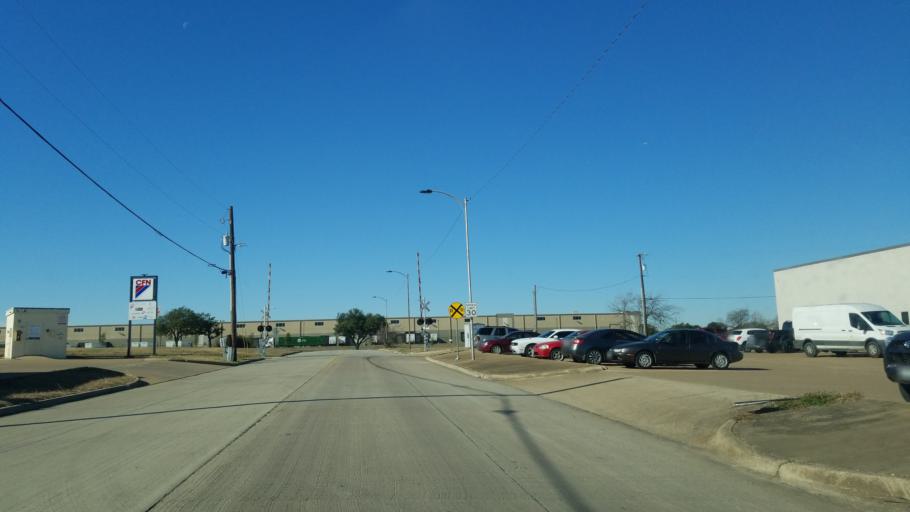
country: US
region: Texas
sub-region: Dallas County
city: Grand Prairie
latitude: 32.7447
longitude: -97.0517
